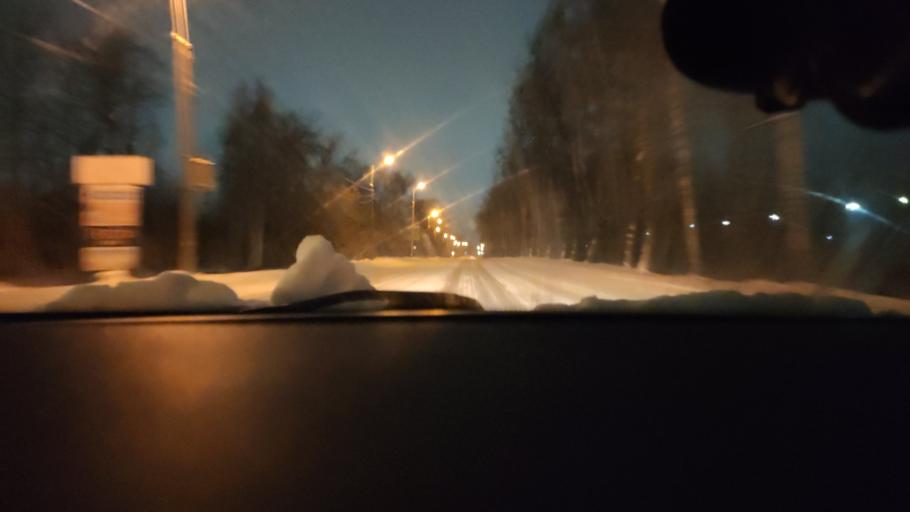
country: RU
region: Perm
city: Krasnokamsk
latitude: 58.0650
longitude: 55.7984
